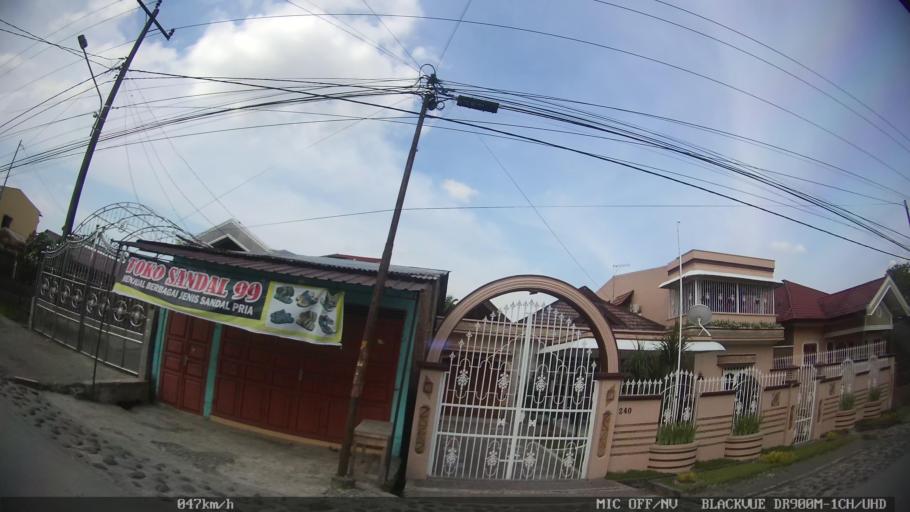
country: ID
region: North Sumatra
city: Binjai
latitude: 3.6336
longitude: 98.4896
